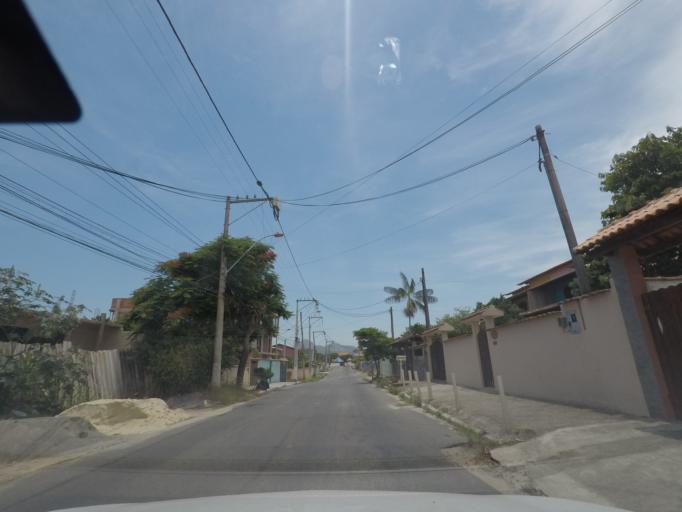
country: BR
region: Rio de Janeiro
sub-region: Marica
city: Marica
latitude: -22.9671
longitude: -42.9606
